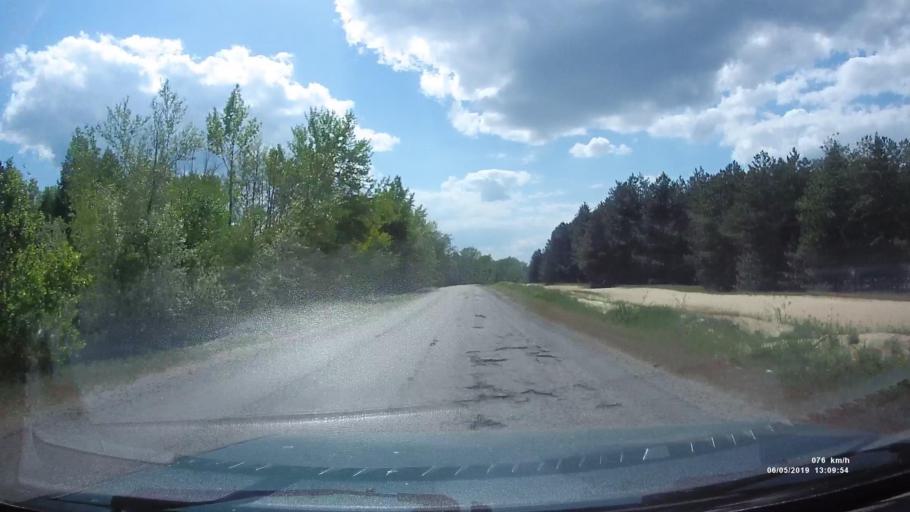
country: RU
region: Rostov
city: Ust'-Donetskiy
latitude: 47.7648
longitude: 40.9781
